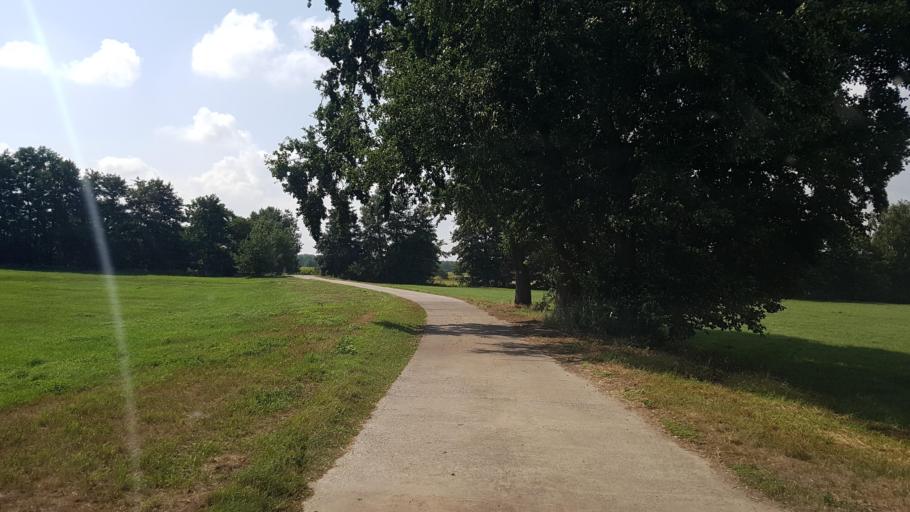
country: DE
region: Brandenburg
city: Borkheide
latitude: 52.1934
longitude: 12.8239
